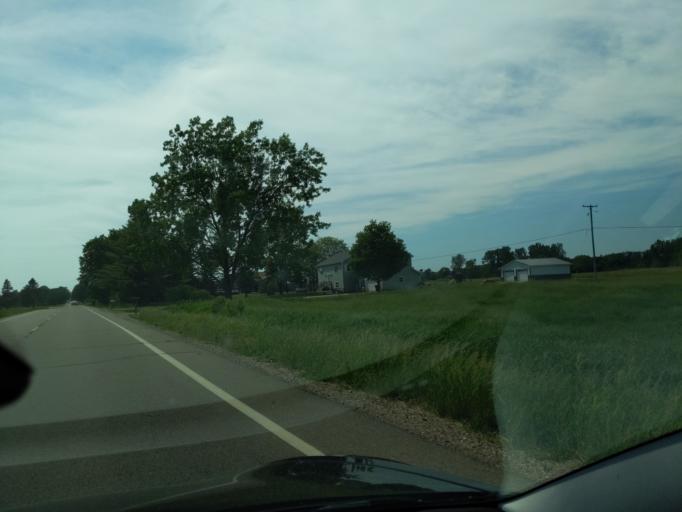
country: US
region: Michigan
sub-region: Eaton County
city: Grand Ledge
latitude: 42.7120
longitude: -84.7863
